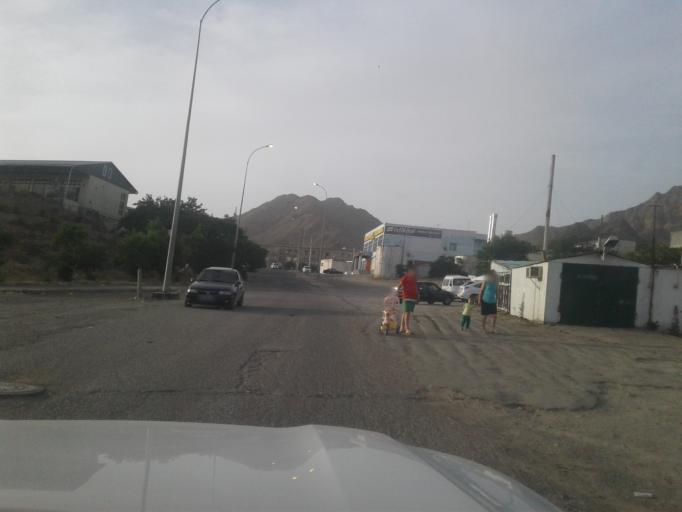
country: TM
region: Balkan
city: Turkmenbasy
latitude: 40.0035
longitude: 52.9648
